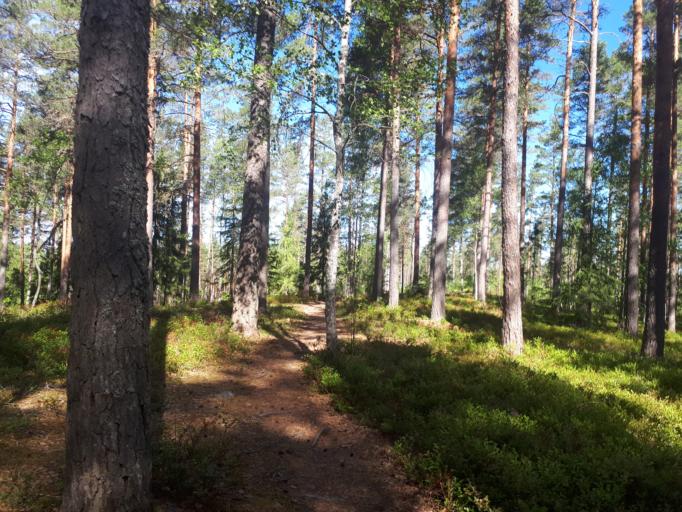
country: SE
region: Soedermanland
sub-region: Katrineholms Kommun
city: Katrineholm
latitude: 59.0953
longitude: 16.1961
